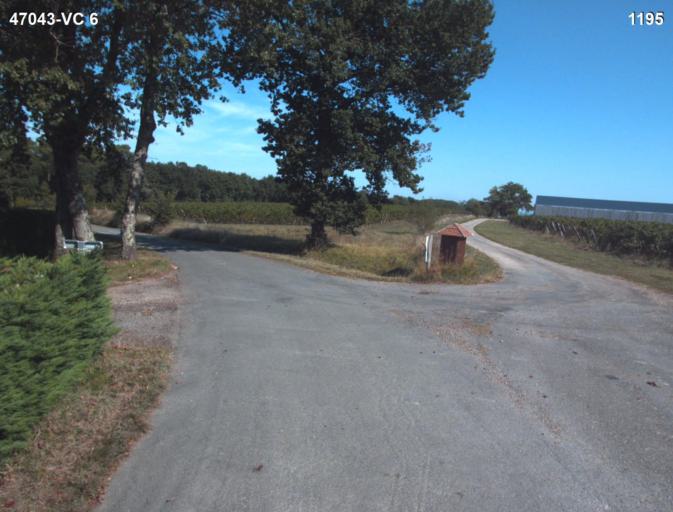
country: FR
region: Aquitaine
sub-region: Departement du Lot-et-Garonne
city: Buzet-sur-Baise
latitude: 44.2358
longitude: 0.3045
